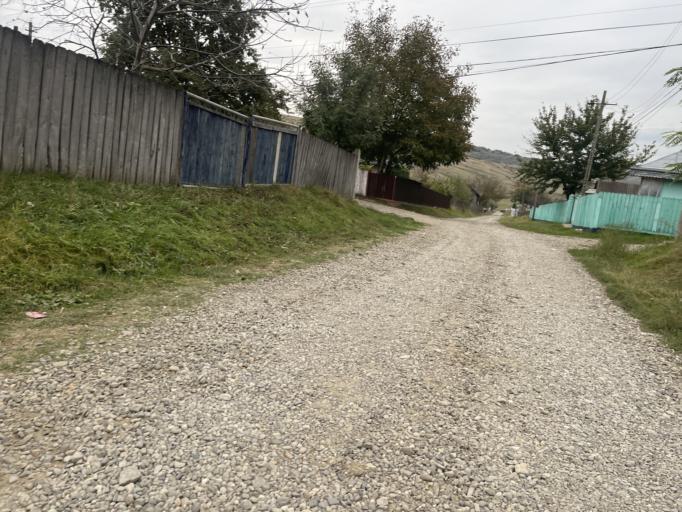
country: RO
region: Iasi
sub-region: Comuna Dumesti
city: Dumesti
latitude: 47.1748
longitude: 27.3441
